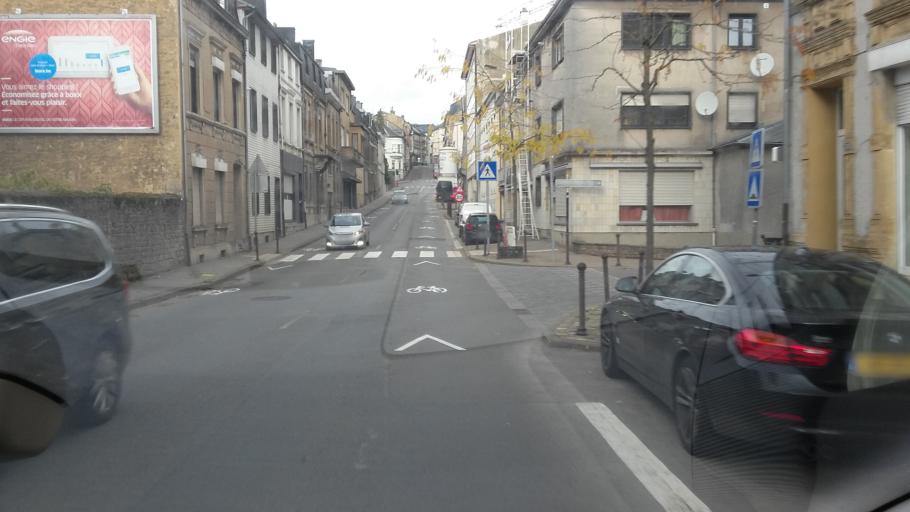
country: BE
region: Wallonia
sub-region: Province du Luxembourg
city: Arlon
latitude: 49.6808
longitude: 5.8194
